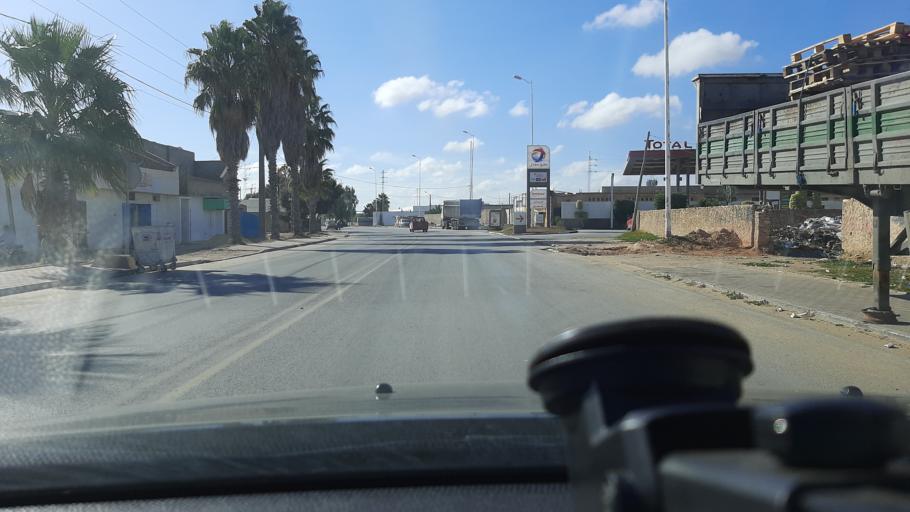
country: TN
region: Safaqis
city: Sfax
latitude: 34.8106
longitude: 10.7080
